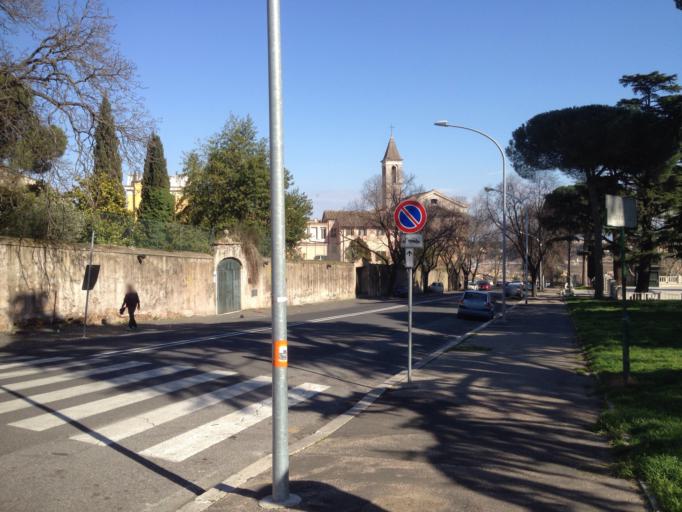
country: VA
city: Vatican City
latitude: 41.8887
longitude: 12.4646
